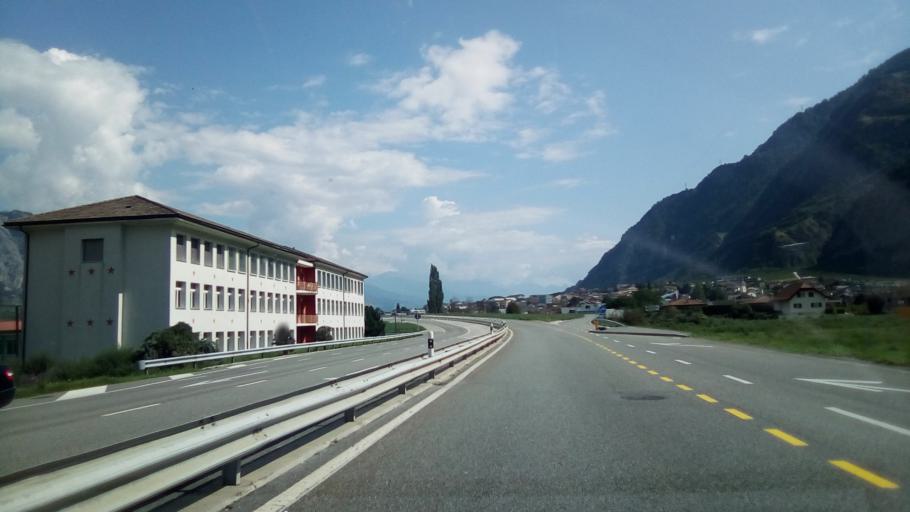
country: CH
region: Valais
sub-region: Martigny District
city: Riddes
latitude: 46.1666
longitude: 7.2109
